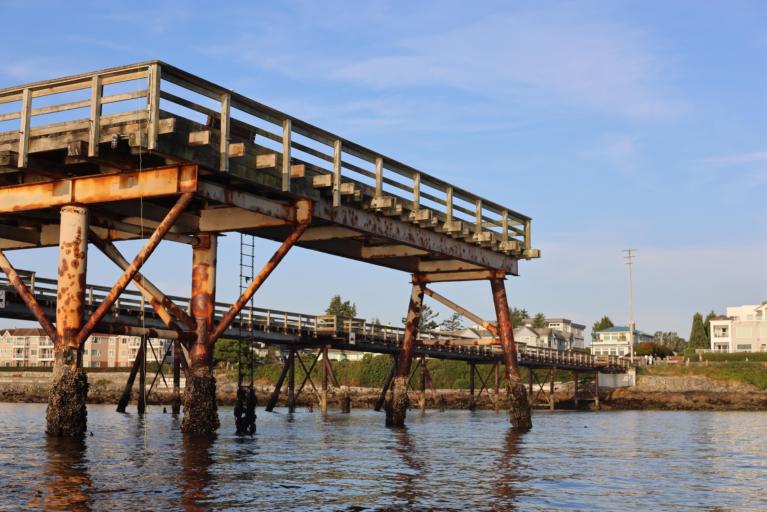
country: CA
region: British Columbia
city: North Saanich
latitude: 48.6480
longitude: -123.3913
